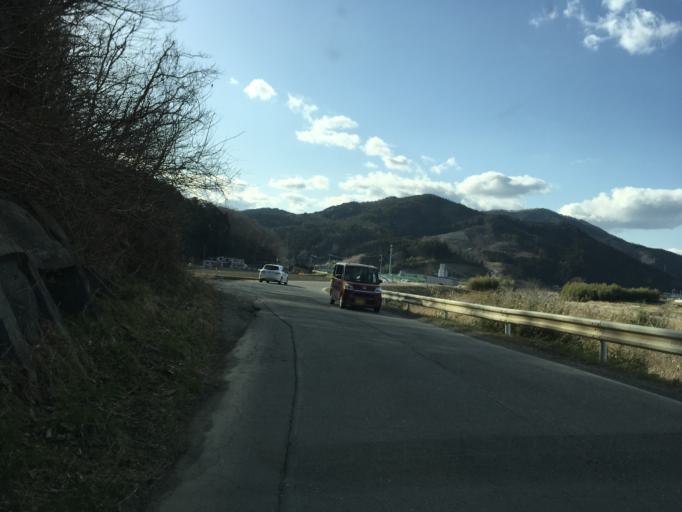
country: JP
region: Iwate
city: Ofunato
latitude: 39.0296
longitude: 141.6083
